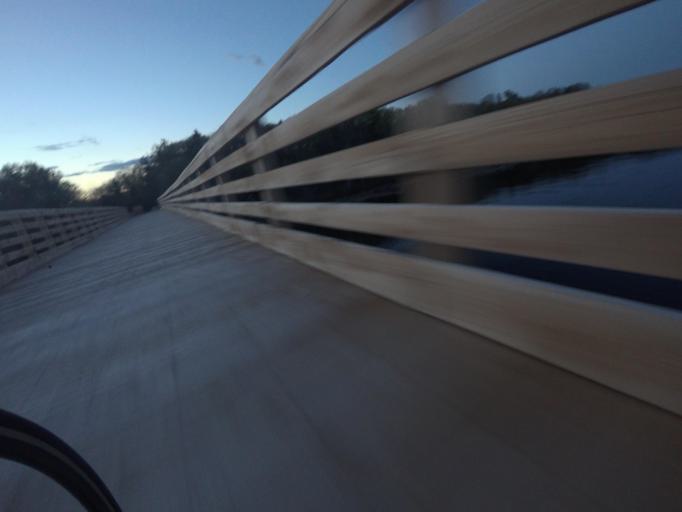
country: CA
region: Ontario
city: Arnprior
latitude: 45.4681
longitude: -76.2869
